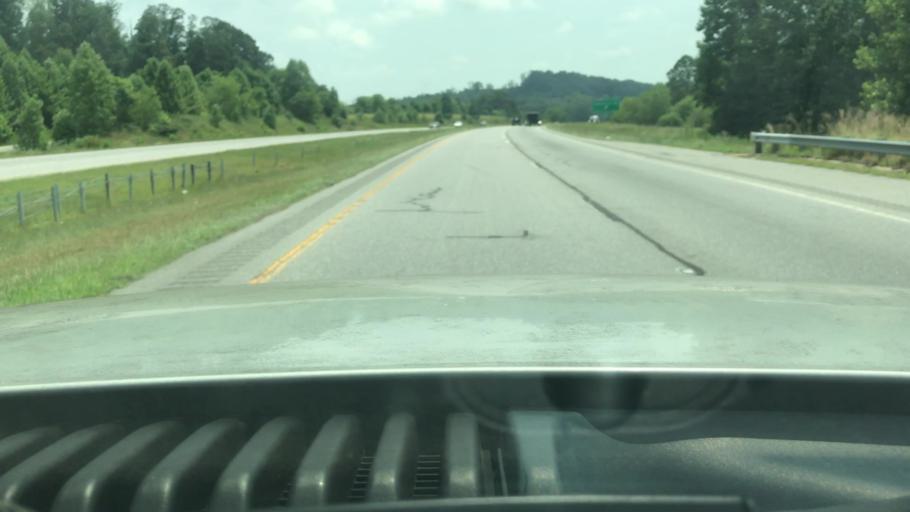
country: US
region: North Carolina
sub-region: Yadkin County
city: Jonesville
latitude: 36.1462
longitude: -80.9043
